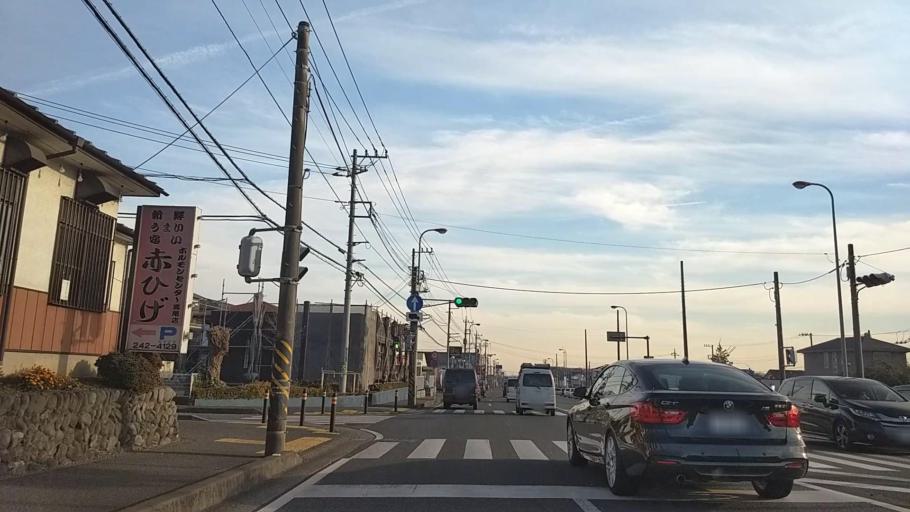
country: JP
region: Kanagawa
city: Atsugi
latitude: 35.4911
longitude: 139.3227
